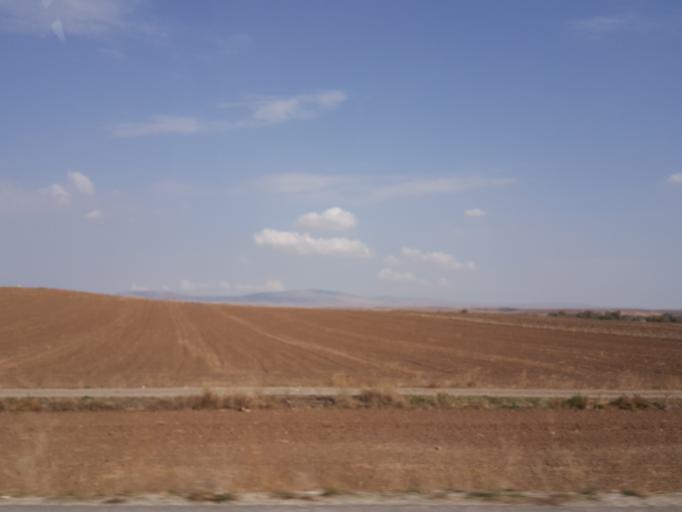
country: TR
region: Corum
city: Alaca
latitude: 40.1463
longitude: 34.8884
